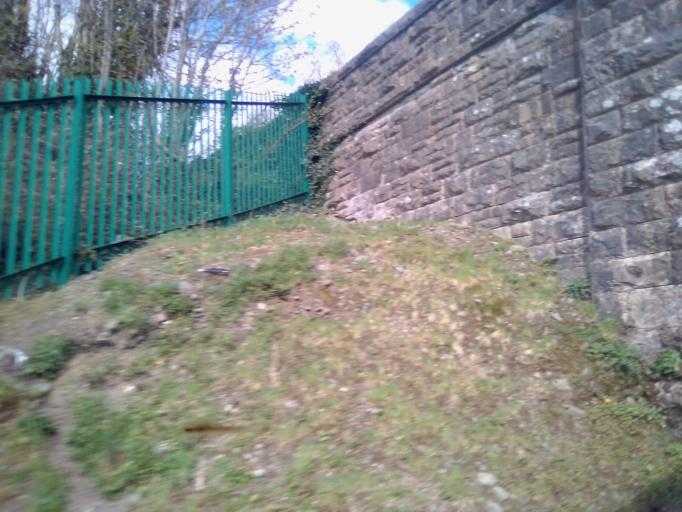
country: IE
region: Munster
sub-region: Ciarrai
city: Cill Airne
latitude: 52.0588
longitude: -9.4929
